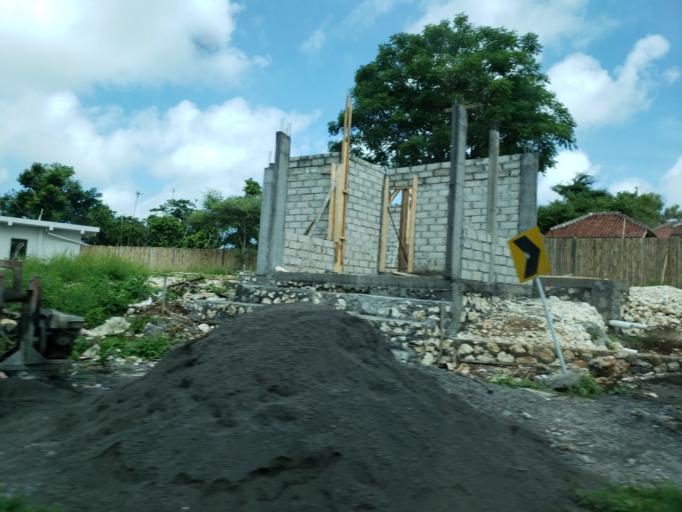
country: ID
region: Bali
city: Pecatu
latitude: -8.8402
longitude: 115.1240
